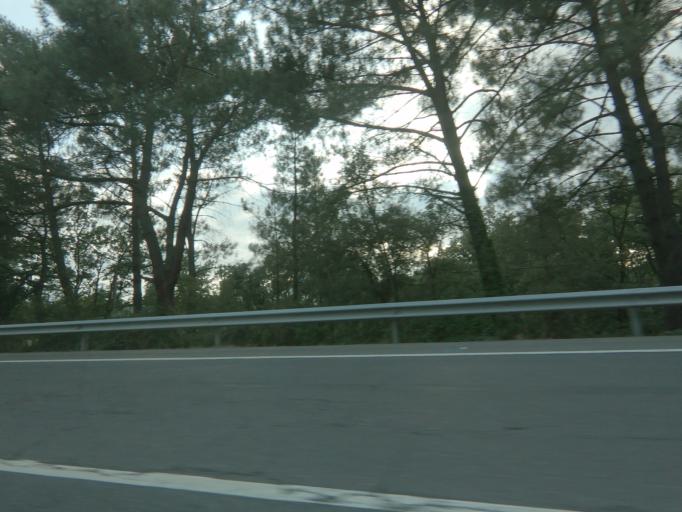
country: ES
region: Galicia
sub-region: Provincia de Ourense
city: Taboadela
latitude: 42.2729
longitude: -7.8378
